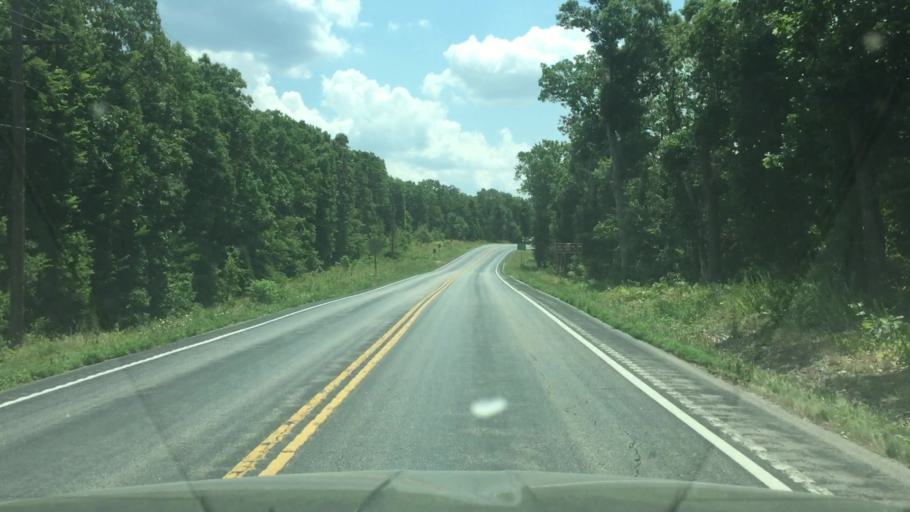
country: US
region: Missouri
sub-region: Camden County
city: Osage Beach
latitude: 38.1319
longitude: -92.5592
